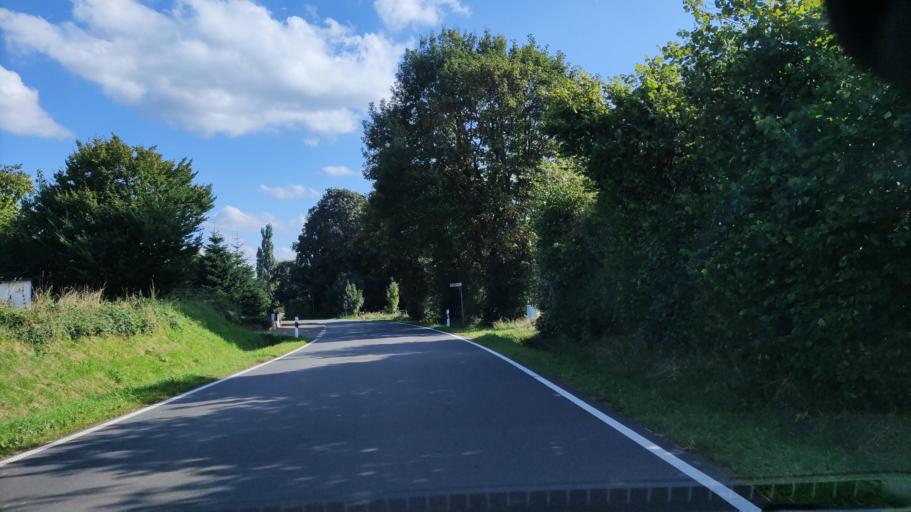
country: DE
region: Schleswig-Holstein
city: Heinkenborstel
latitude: 54.1326
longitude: 9.7461
